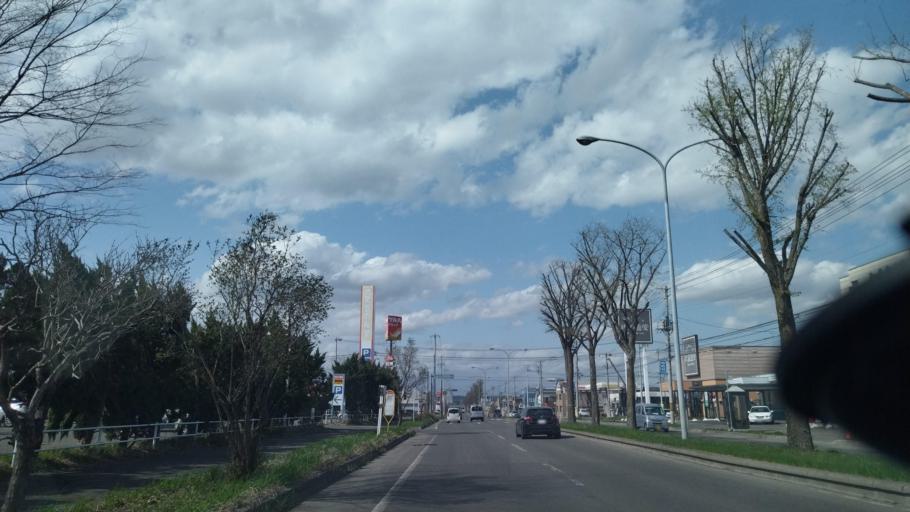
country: JP
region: Hokkaido
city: Obihiro
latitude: 42.9116
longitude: 143.1452
